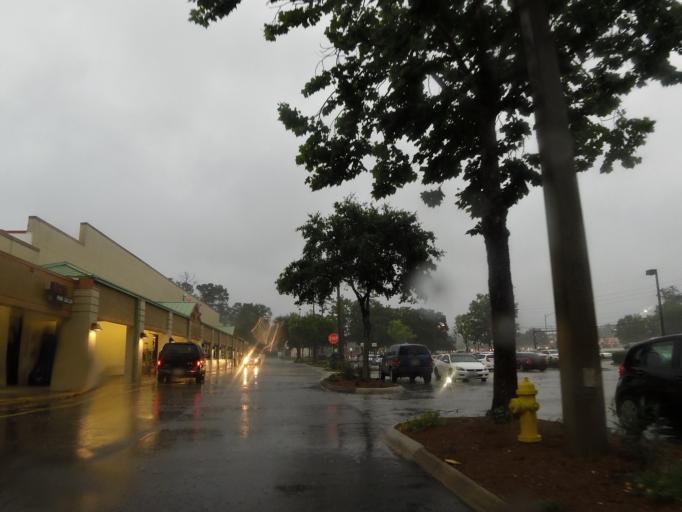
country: US
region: Florida
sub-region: Duval County
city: Jacksonville
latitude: 30.2880
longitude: -81.5656
